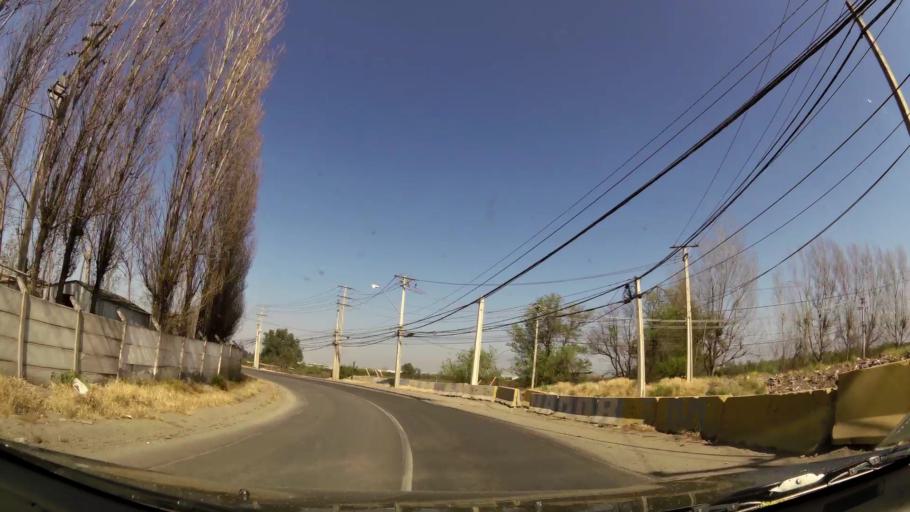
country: CL
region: Santiago Metropolitan
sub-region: Provincia de Chacabuco
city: Chicureo Abajo
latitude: -33.3171
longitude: -70.7109
